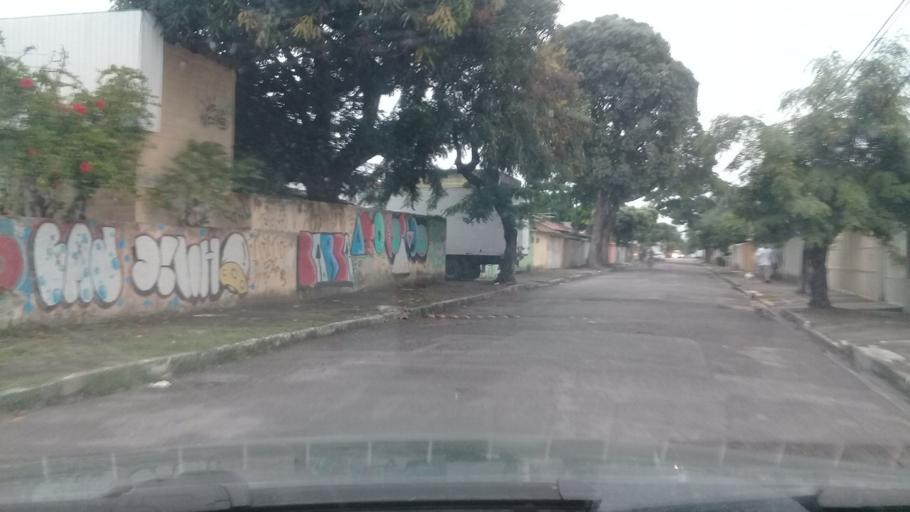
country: BR
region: Pernambuco
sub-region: Recife
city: Recife
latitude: -8.1120
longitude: -34.9233
